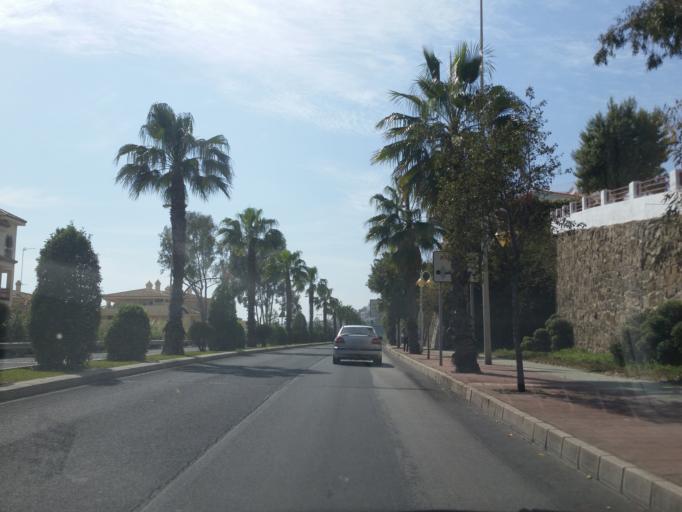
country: ES
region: Andalusia
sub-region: Provincia de Malaga
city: Benalmadena
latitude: 36.5813
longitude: -4.5514
